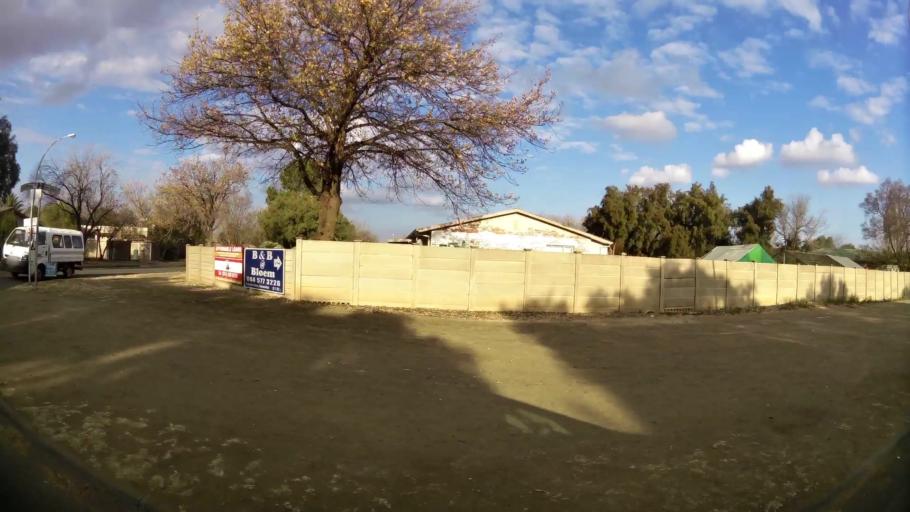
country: ZA
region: Orange Free State
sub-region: Mangaung Metropolitan Municipality
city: Bloemfontein
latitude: -29.0984
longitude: 26.1884
